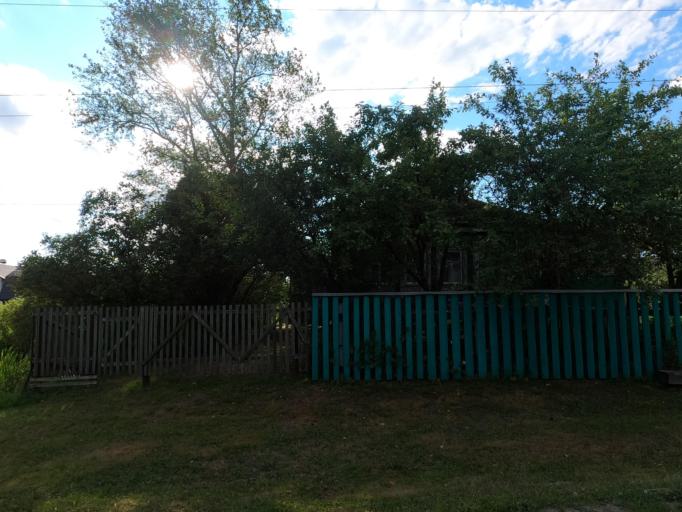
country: RU
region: Moskovskaya
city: Konobeyevo
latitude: 55.4096
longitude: 38.7180
